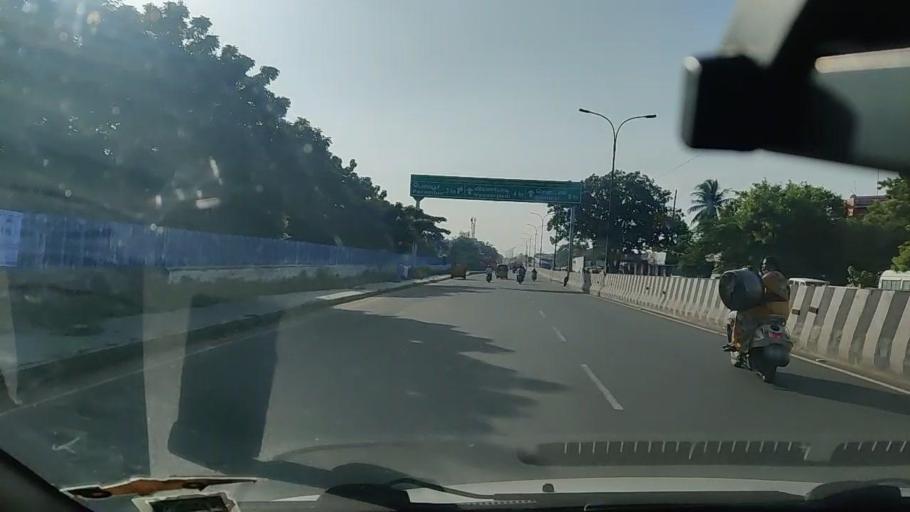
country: IN
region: Tamil Nadu
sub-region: Thiruvallur
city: Chinnasekkadu
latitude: 13.1322
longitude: 80.2370
